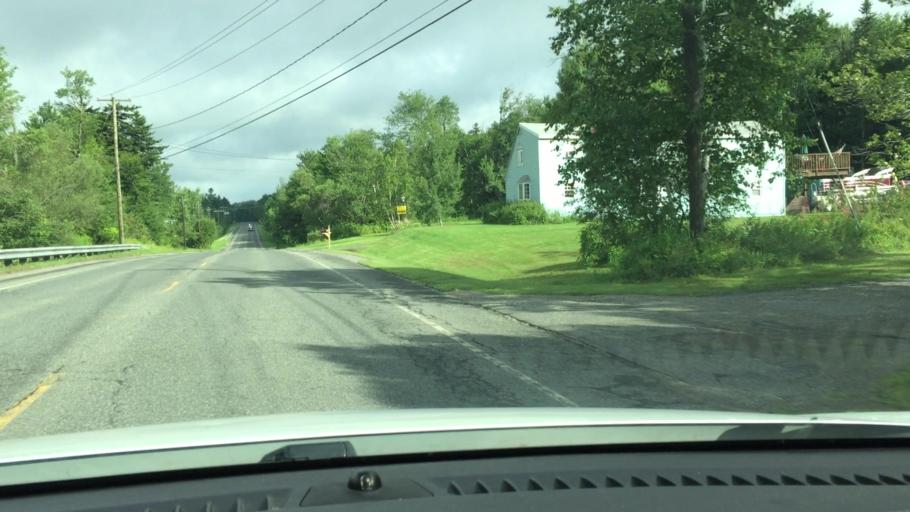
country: US
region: Massachusetts
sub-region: Berkshire County
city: Hinsdale
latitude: 42.4403
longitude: -73.0494
